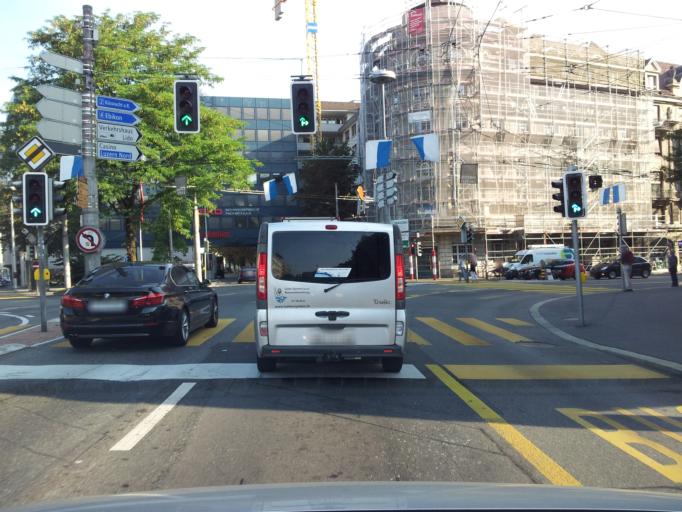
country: CH
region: Lucerne
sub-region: Lucerne-Stadt District
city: Luzern
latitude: 47.0476
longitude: 8.3040
